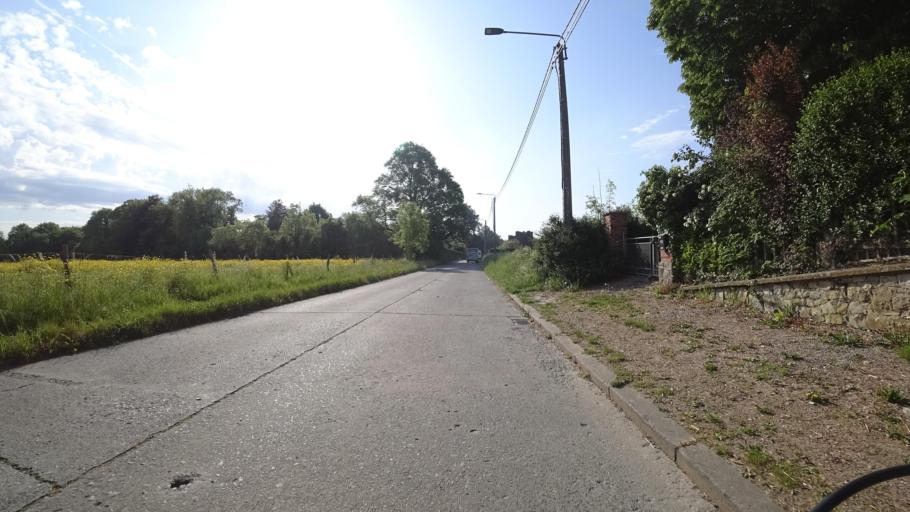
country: BE
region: Wallonia
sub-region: Province de Namur
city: Namur
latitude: 50.4800
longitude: 4.8290
